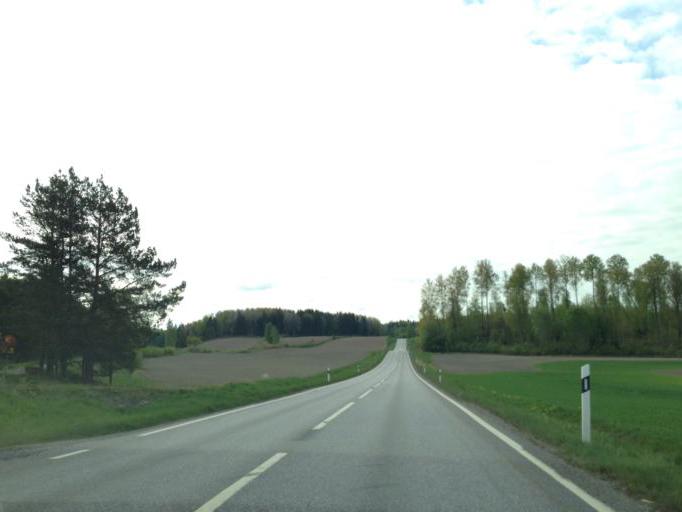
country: SE
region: Soedermanland
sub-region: Flens Kommun
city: Malmkoping
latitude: 59.1132
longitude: 16.7638
